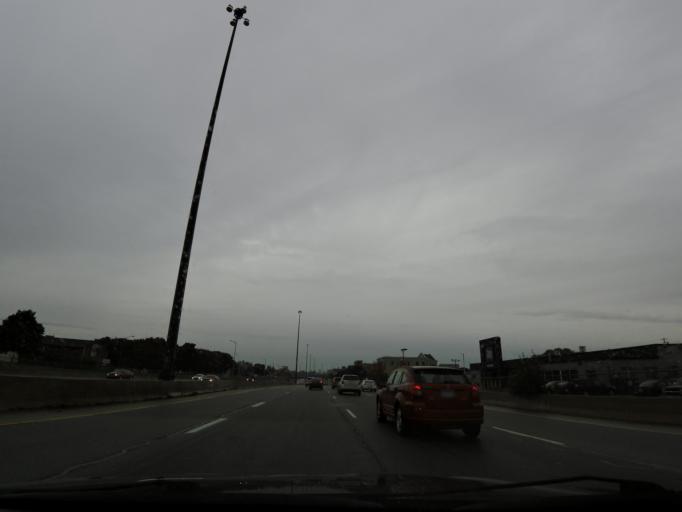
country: CA
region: Ontario
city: Kitchener
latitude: 43.4322
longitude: -80.4438
